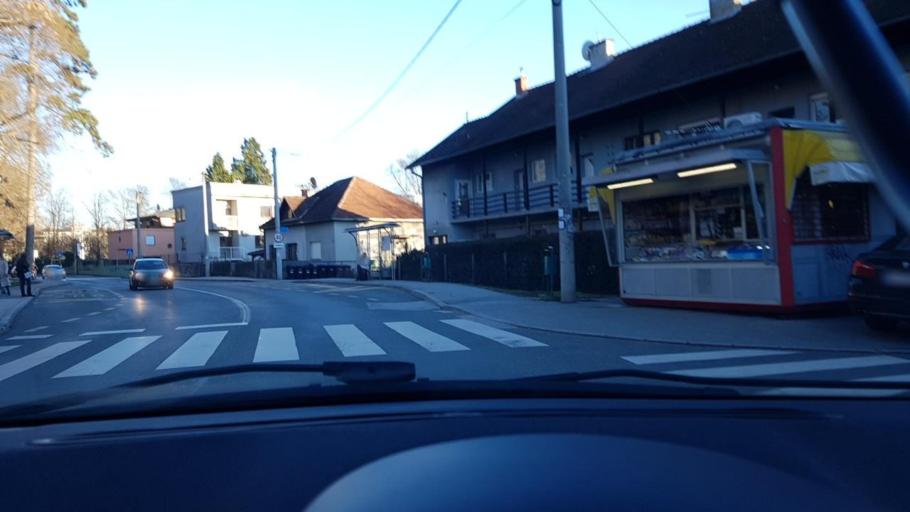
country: HR
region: Grad Zagreb
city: Stenjevec
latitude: 45.8151
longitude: 15.8948
